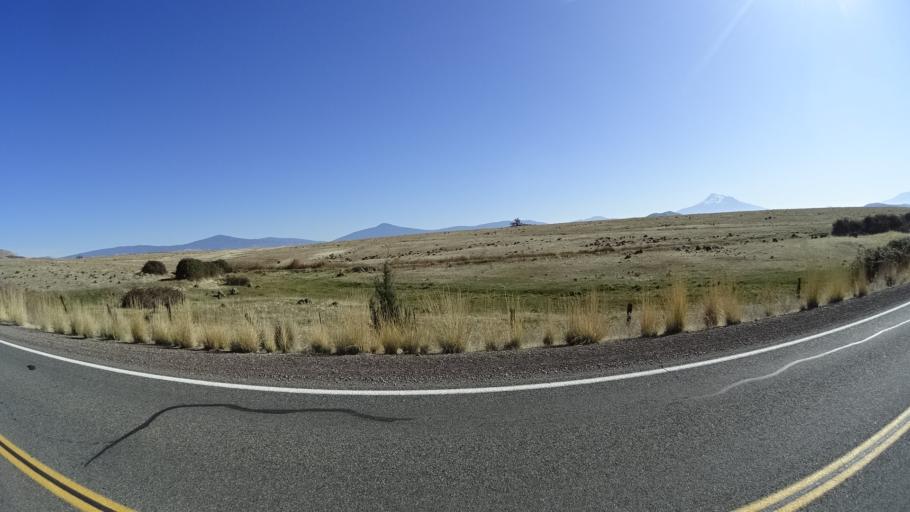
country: US
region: California
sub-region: Siskiyou County
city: Montague
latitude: 41.7528
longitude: -122.5674
